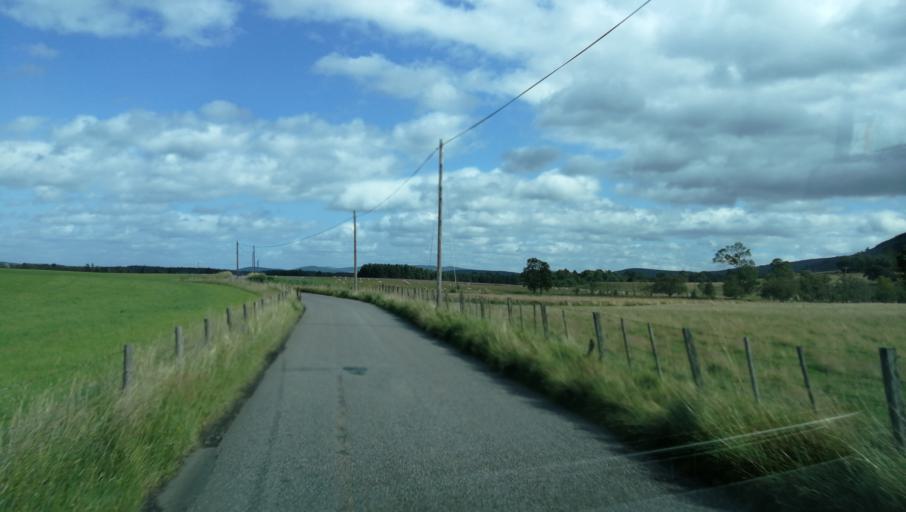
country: GB
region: Scotland
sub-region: Highland
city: Aviemore
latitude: 57.2090
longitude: -3.7771
